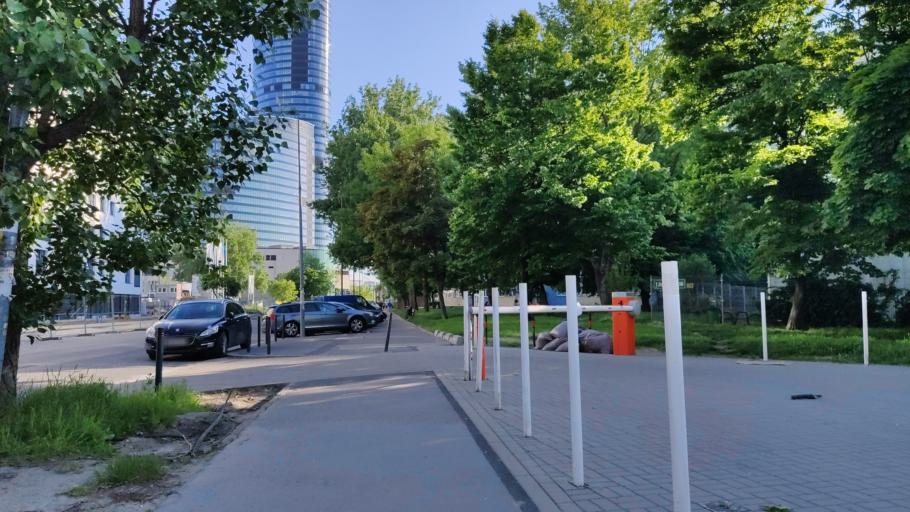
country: PL
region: Lower Silesian Voivodeship
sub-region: Powiat wroclawski
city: Wroclaw
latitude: 51.0975
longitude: 17.0218
